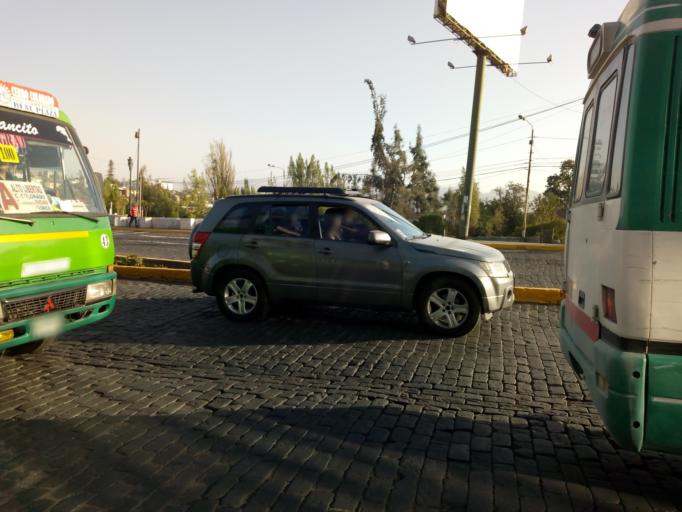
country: PE
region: Arequipa
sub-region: Provincia de Arequipa
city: Arequipa
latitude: -16.3923
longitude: -71.5400
